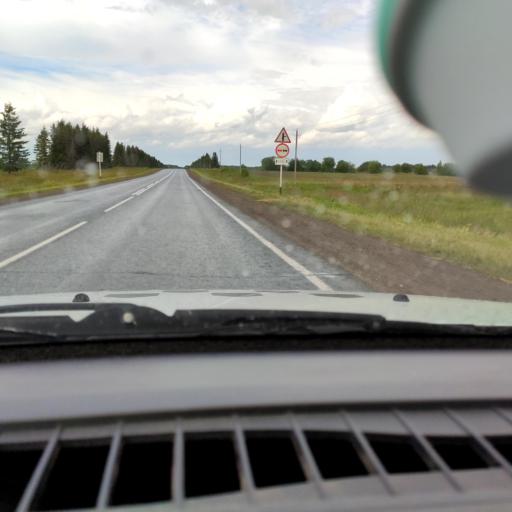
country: RU
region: Perm
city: Orda
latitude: 57.2061
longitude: 56.9269
